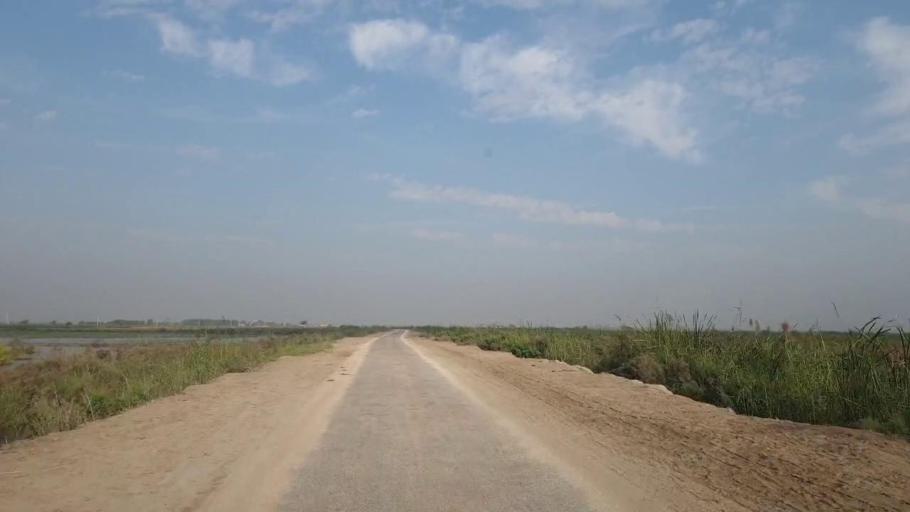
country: PK
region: Sindh
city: Tando Bago
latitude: 24.8486
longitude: 68.9724
